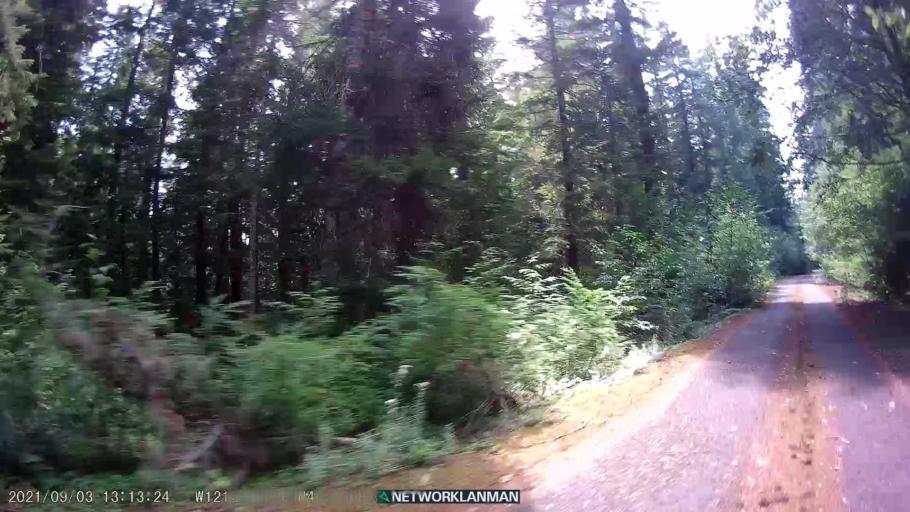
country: US
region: Washington
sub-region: Skamania County
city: Carson
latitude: 46.1948
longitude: -121.7907
